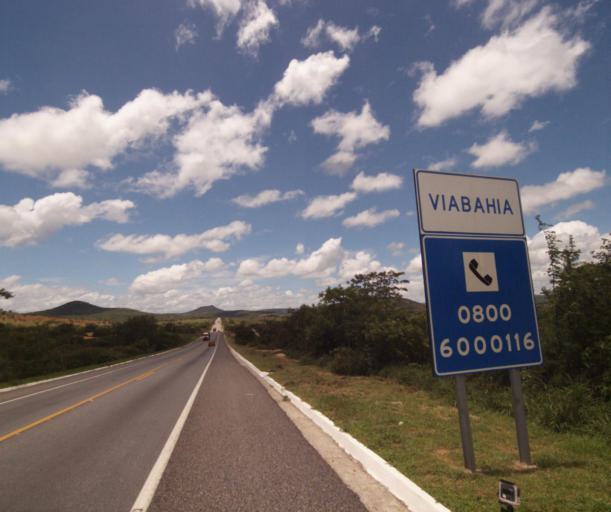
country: BR
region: Bahia
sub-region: Pocoes
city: Pocoes
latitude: -14.3804
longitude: -40.3488
